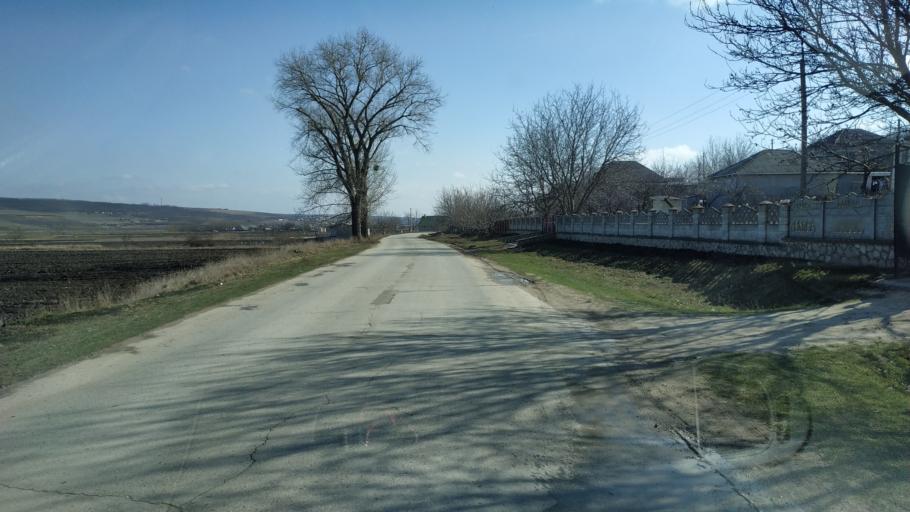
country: MD
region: Hincesti
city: Hincesti
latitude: 46.9382
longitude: 28.6340
